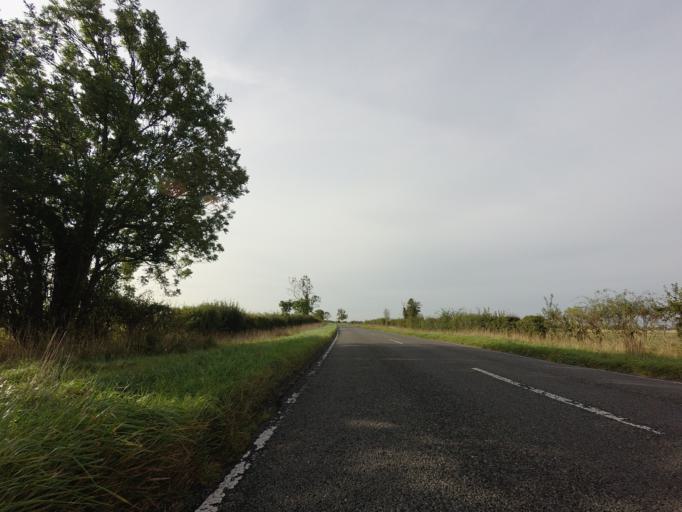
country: GB
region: England
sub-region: Cambridgeshire
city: Harston
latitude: 52.1060
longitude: 0.0860
